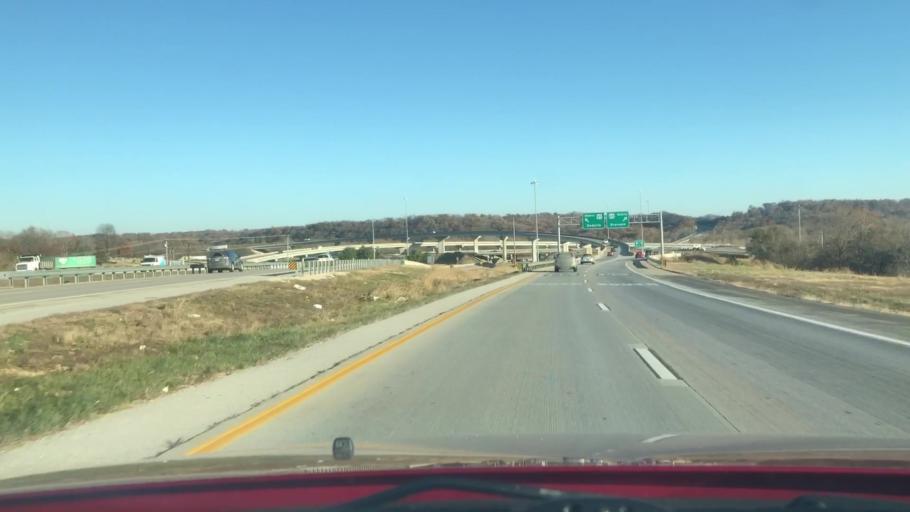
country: US
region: Missouri
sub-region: Christian County
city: Nixa
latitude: 37.1299
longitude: -93.2370
